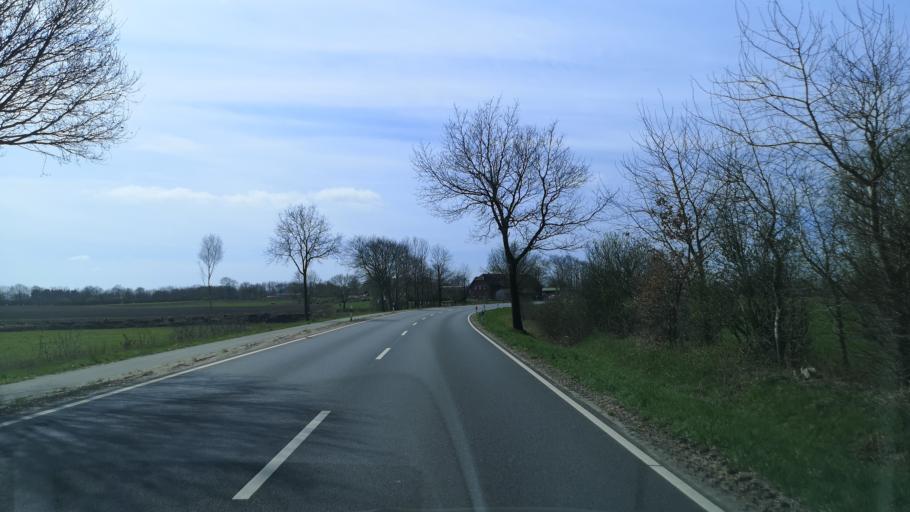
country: DE
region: Schleswig-Holstein
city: Hamdorf
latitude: 54.2254
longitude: 9.4974
